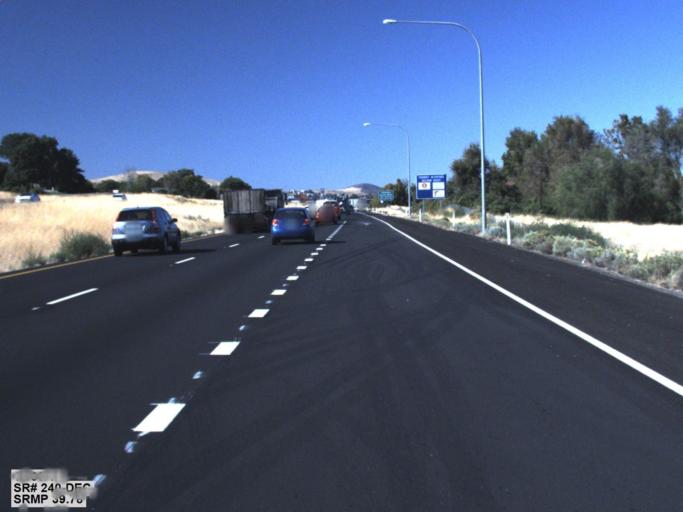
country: US
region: Washington
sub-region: Franklin County
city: West Pasco
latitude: 46.2312
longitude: -119.2051
